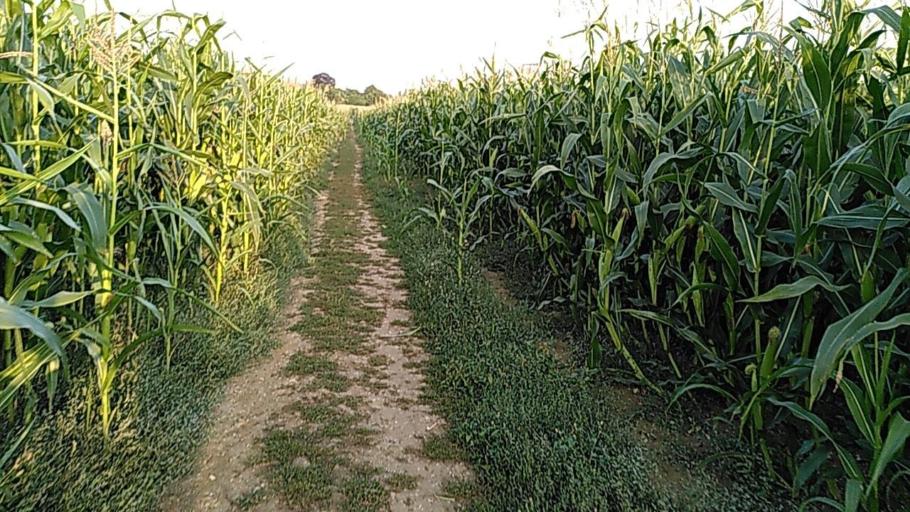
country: GB
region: England
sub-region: Oxfordshire
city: Sonning Common
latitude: 51.4924
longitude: -0.9519
